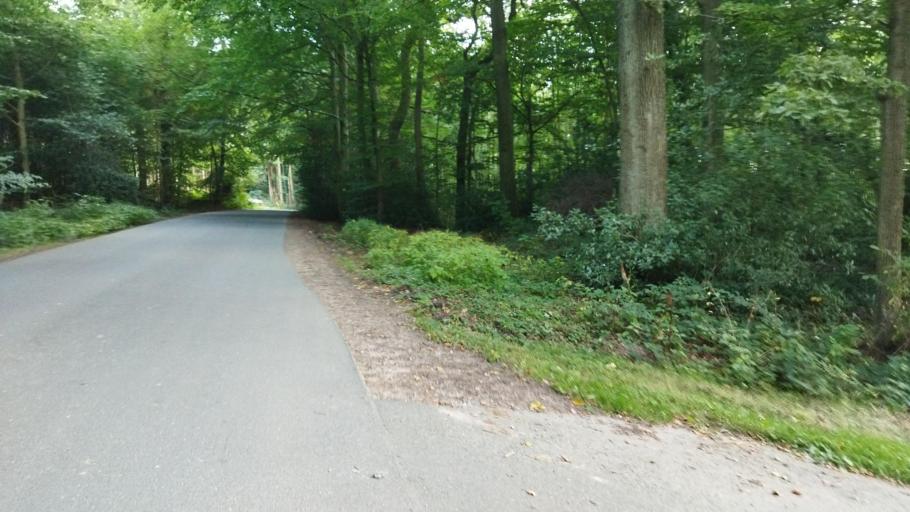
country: DE
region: Lower Saxony
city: Hagen
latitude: 52.1875
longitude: 8.0078
